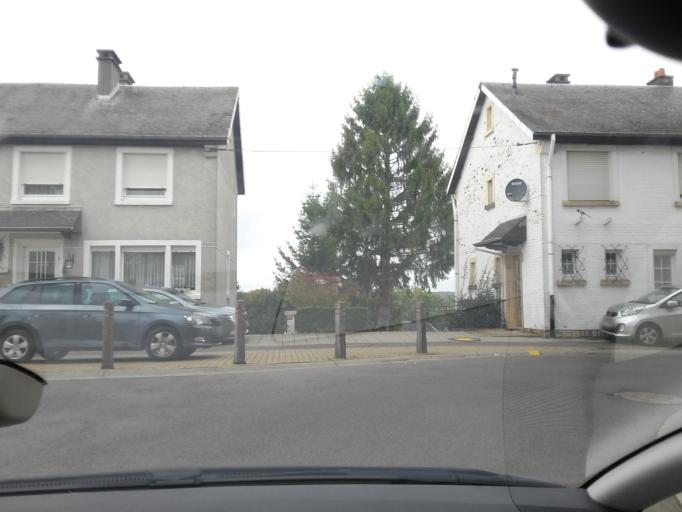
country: BE
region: Wallonia
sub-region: Province du Luxembourg
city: Arlon
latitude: 49.6892
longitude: 5.8040
